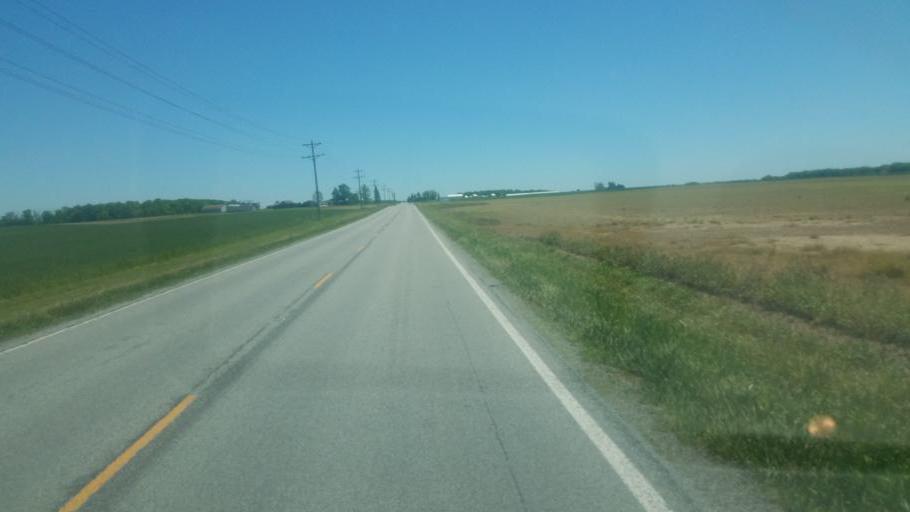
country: US
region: Ohio
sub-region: Miami County
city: Piqua
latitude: 40.2252
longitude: -84.3171
